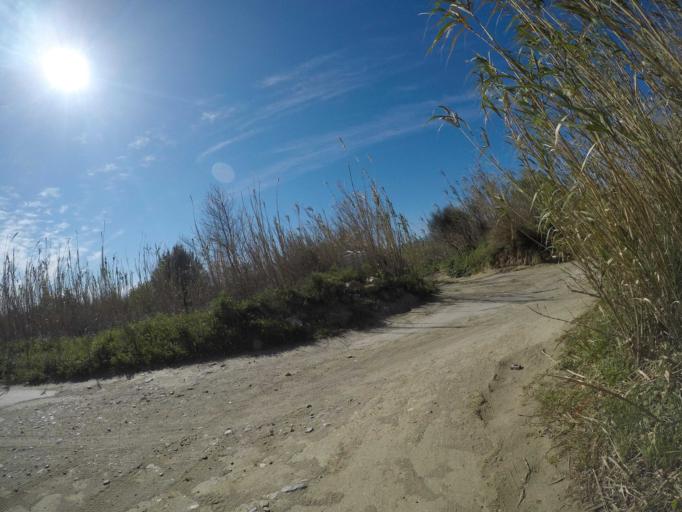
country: FR
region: Languedoc-Roussillon
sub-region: Departement des Pyrenees-Orientales
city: Millas
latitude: 42.7014
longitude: 2.6849
